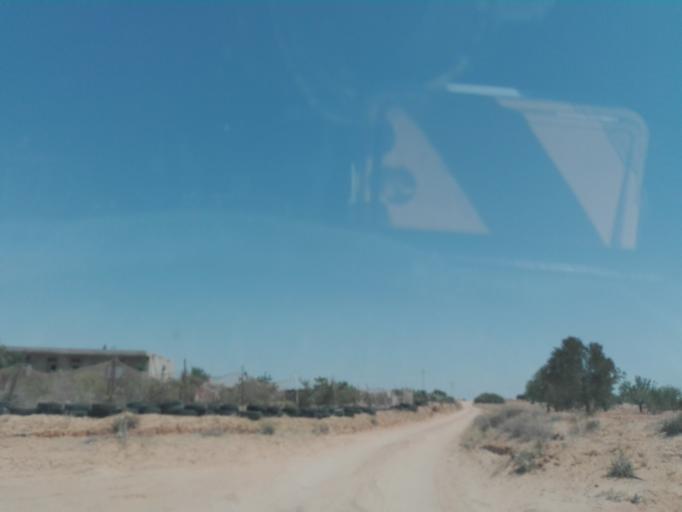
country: TN
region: Safaqis
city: Bi'r `Ali Bin Khalifah
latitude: 34.6726
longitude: 10.2343
